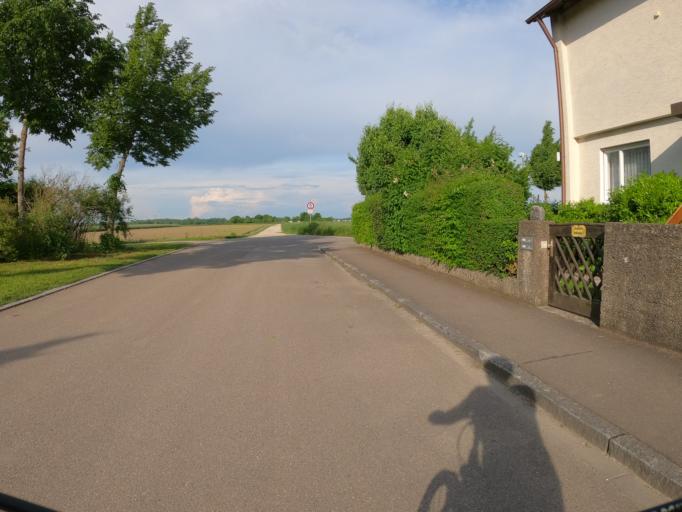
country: DE
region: Bavaria
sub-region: Swabia
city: Neu-Ulm
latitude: 48.4152
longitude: 10.0422
